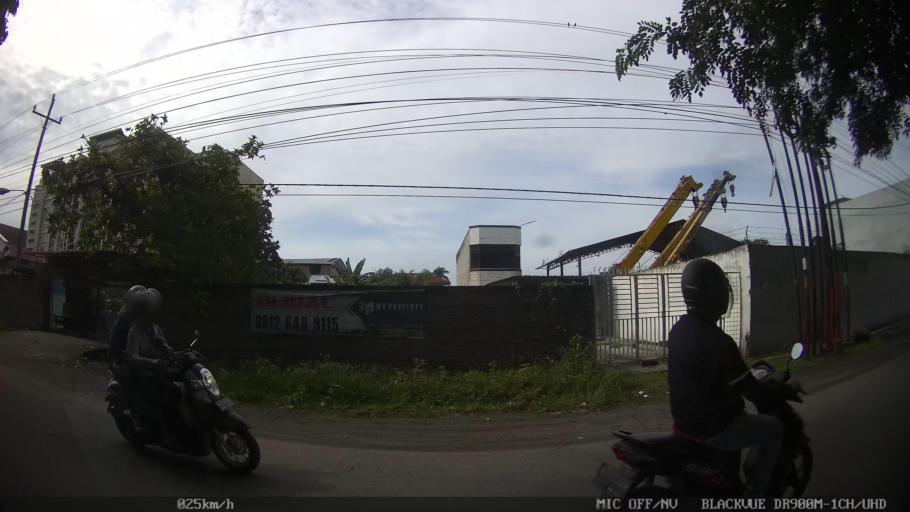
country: ID
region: North Sumatra
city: Medan
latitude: 3.6285
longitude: 98.7054
